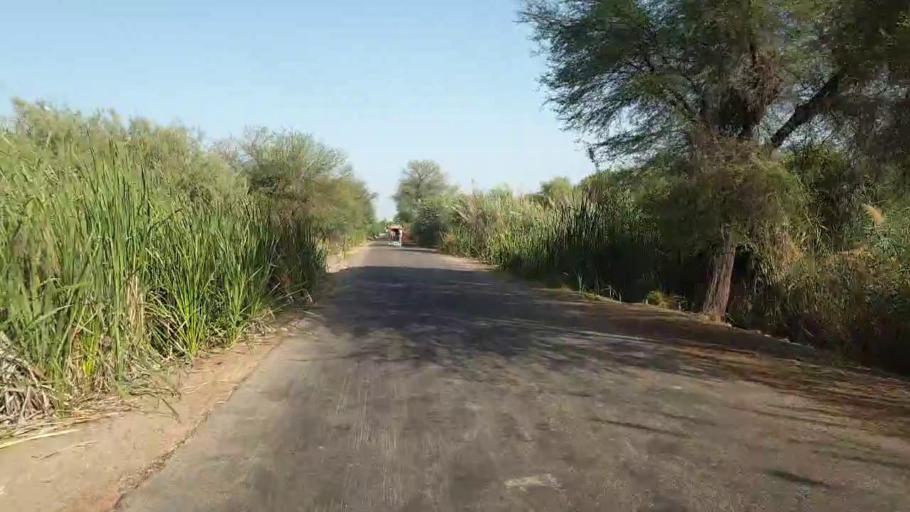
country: PK
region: Sindh
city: Nawabshah
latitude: 26.3805
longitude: 68.4585
